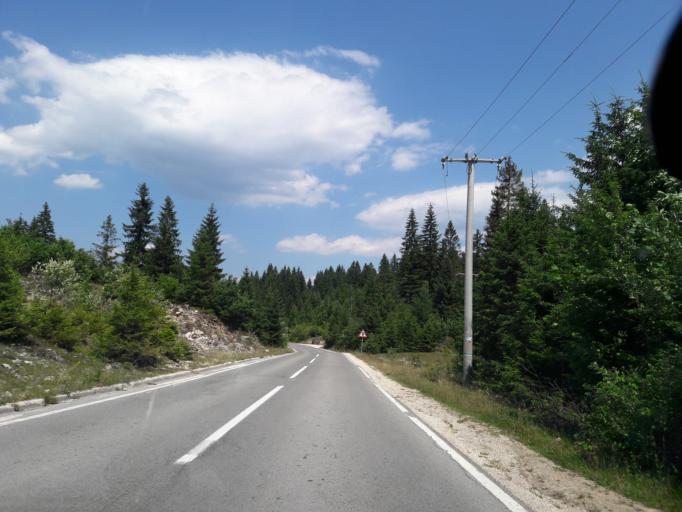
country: BA
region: Republika Srpska
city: Sipovo
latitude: 44.1241
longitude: 17.1816
